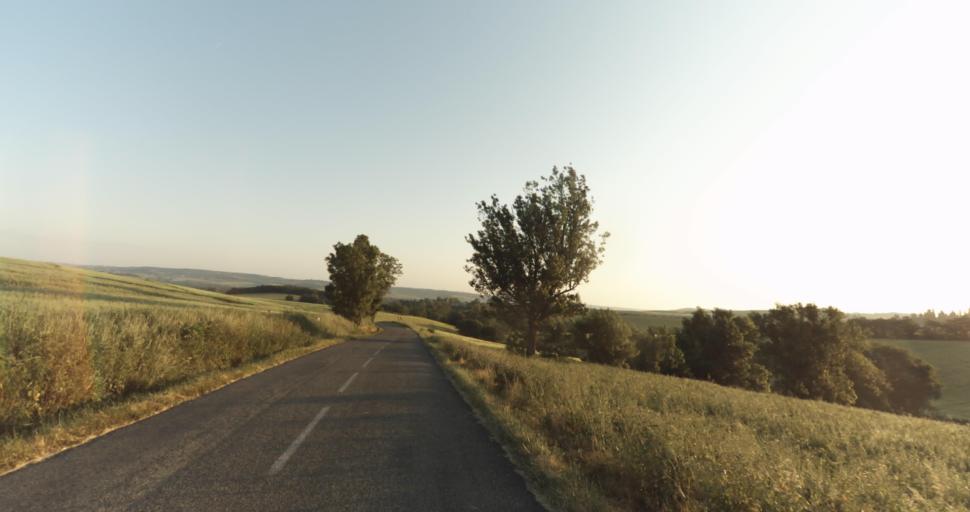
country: FR
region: Midi-Pyrenees
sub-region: Departement du Gers
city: Pujaudran
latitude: 43.6181
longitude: 1.1567
